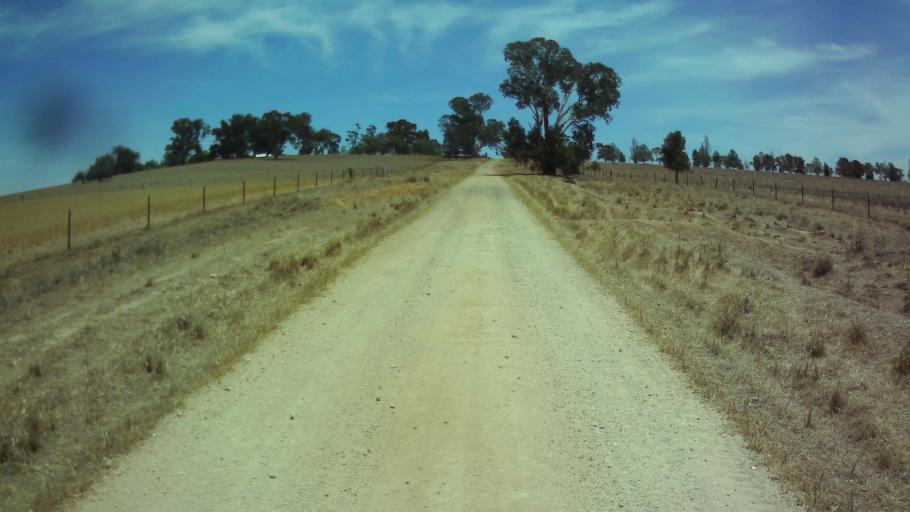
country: AU
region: New South Wales
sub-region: Weddin
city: Grenfell
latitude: -34.0201
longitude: 148.4278
